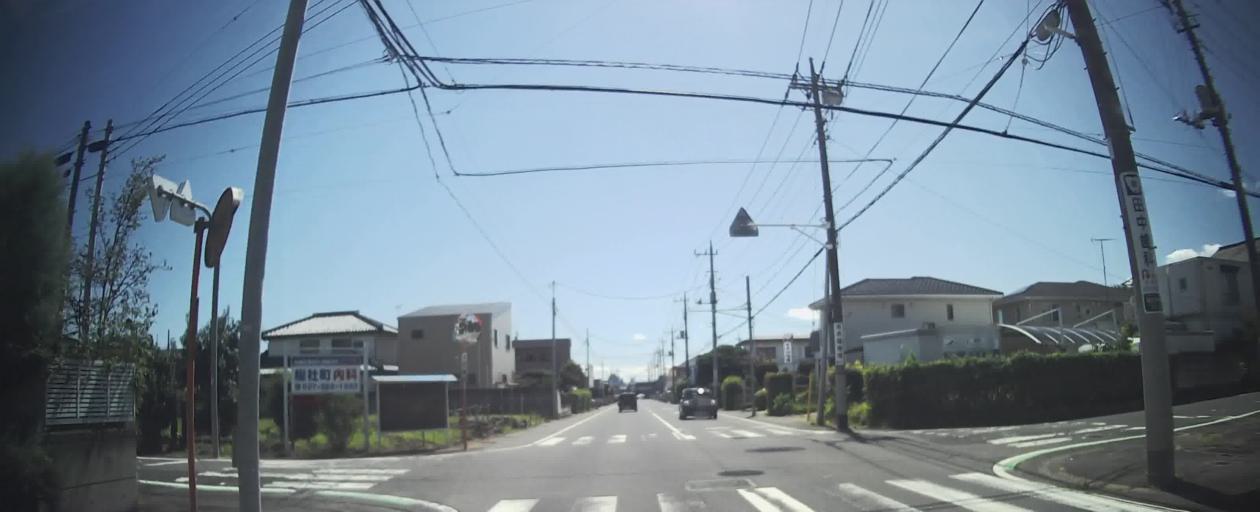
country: JP
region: Gunma
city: Maebashi-shi
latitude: 36.4055
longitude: 139.0414
